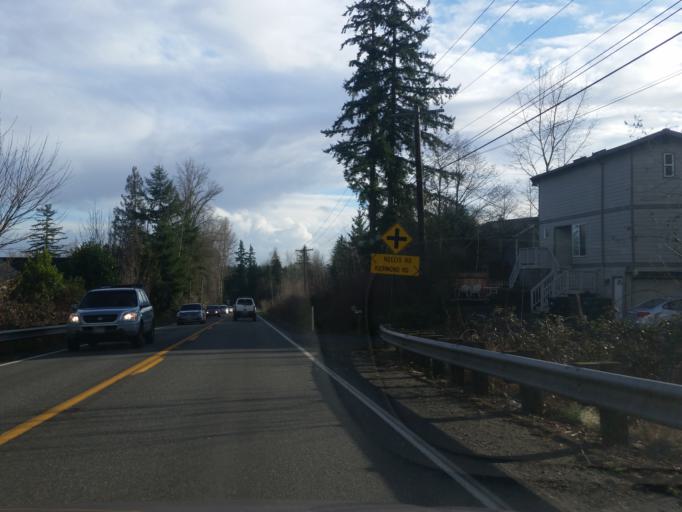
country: US
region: Washington
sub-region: Snohomish County
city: Martha Lake
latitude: 47.8140
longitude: -122.2280
